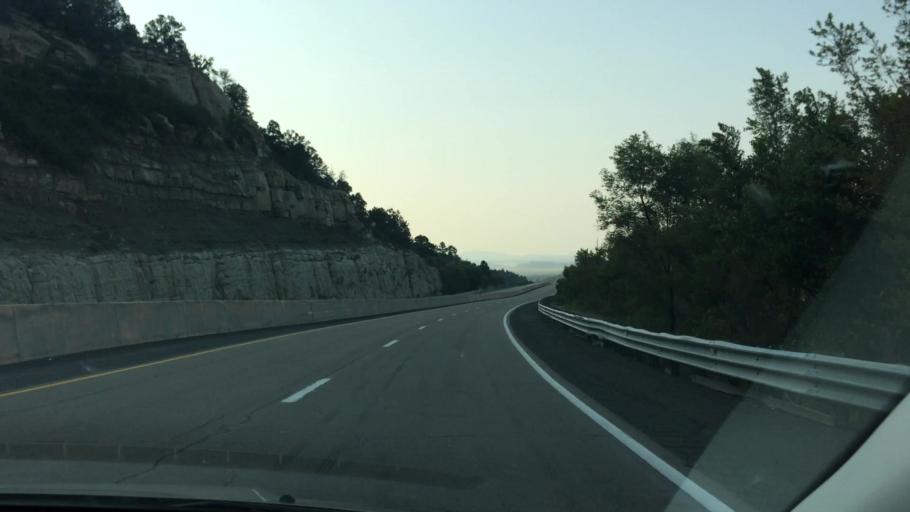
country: US
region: New Mexico
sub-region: Colfax County
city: Raton
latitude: 36.9314
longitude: -104.4585
